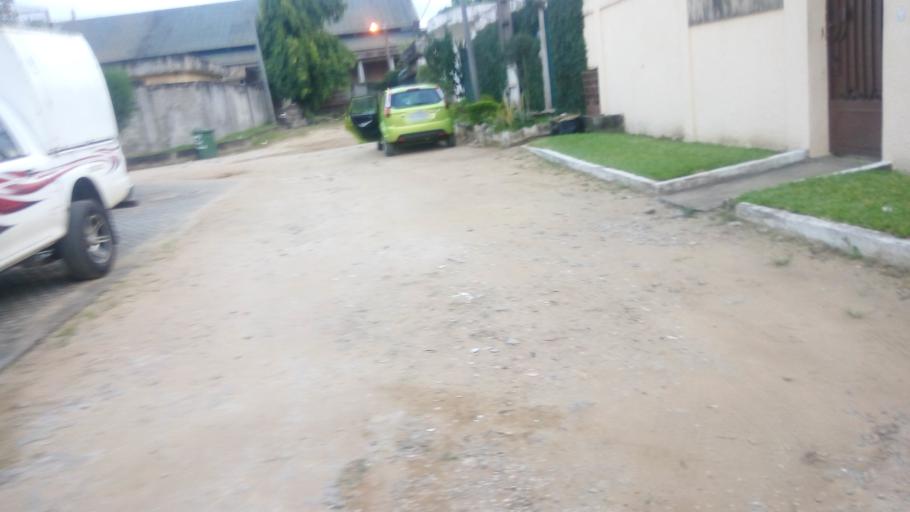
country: CI
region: Lagunes
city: Abobo
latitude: 5.4090
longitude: -3.9905
